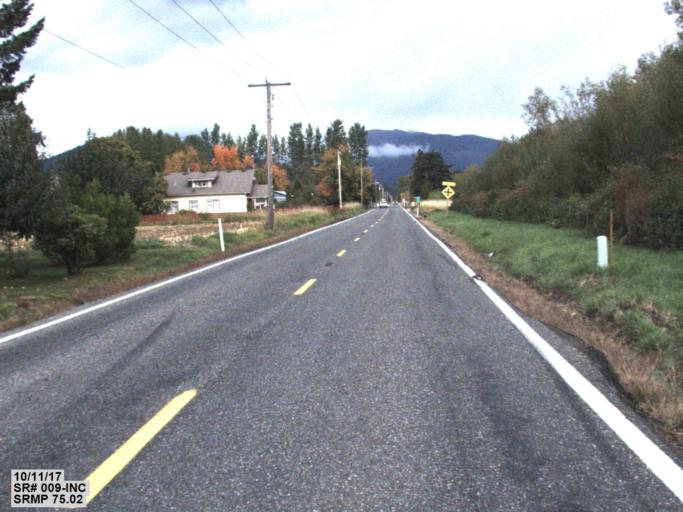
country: US
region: Washington
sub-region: Whatcom County
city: Sudden Valley
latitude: 48.7574
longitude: -122.2019
